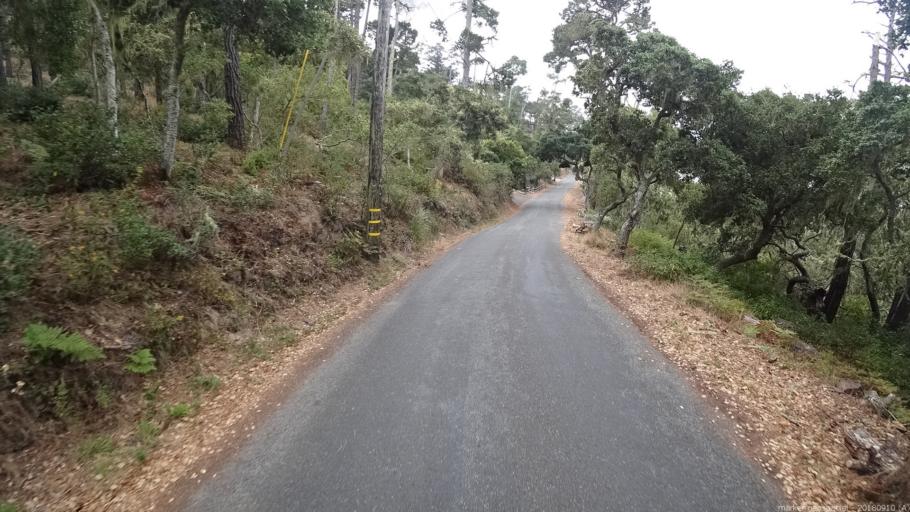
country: US
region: California
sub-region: Monterey County
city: Carmel-by-the-Sea
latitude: 36.5014
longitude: -121.9317
